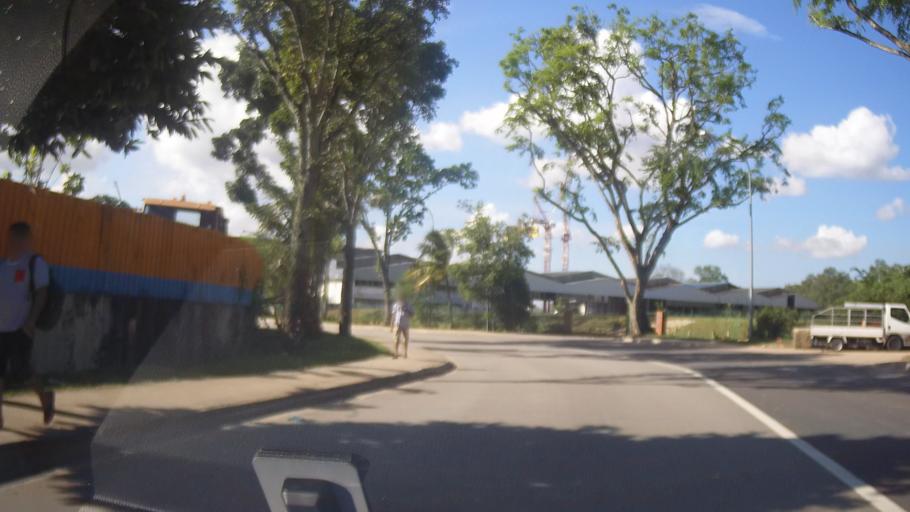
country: MY
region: Johor
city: Johor Bahru
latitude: 1.4336
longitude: 103.7582
